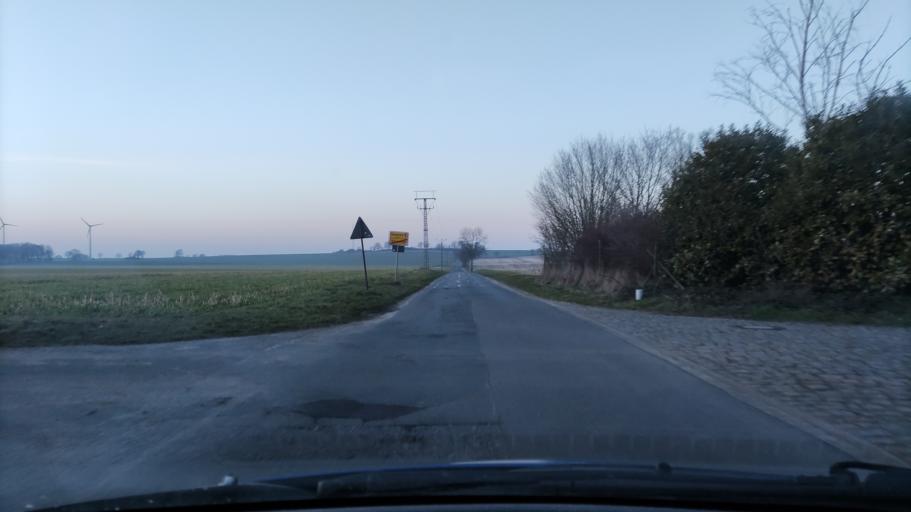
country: DE
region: Lower Saxony
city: Barum
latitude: 53.0396
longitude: 10.4817
